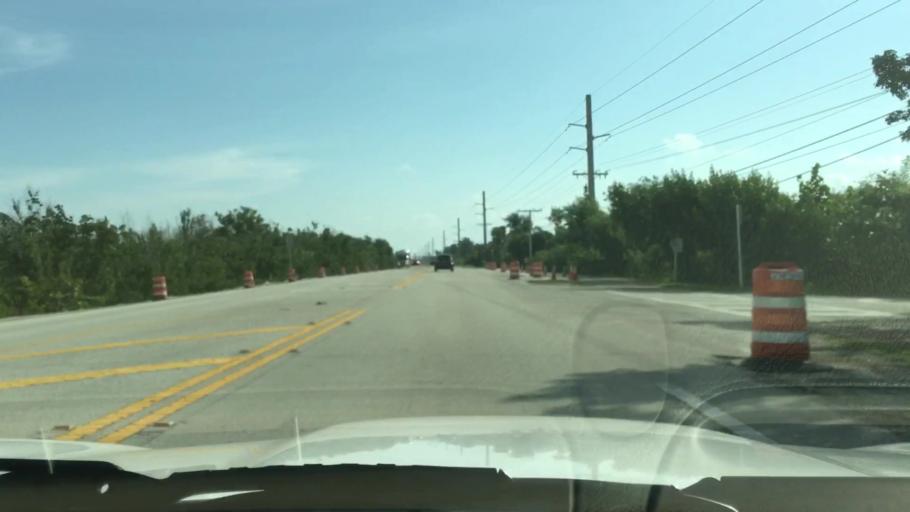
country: US
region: Florida
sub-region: Monroe County
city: Cudjoe Key
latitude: 24.6624
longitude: -81.4611
